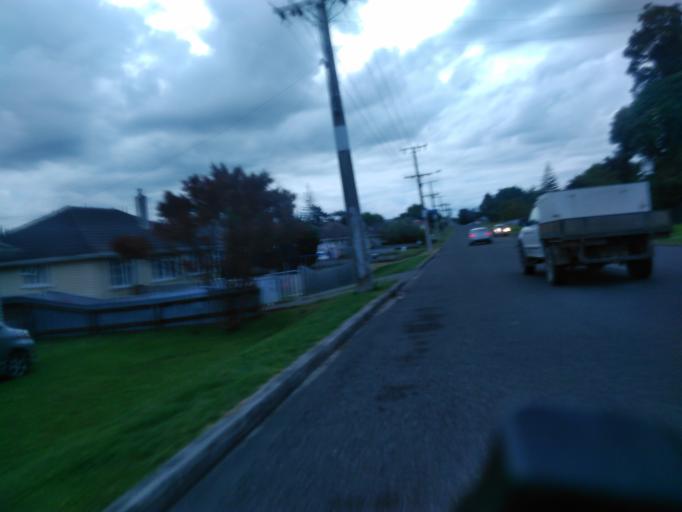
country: NZ
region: Gisborne
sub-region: Gisborne District
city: Gisborne
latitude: -38.6468
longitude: 178.0108
